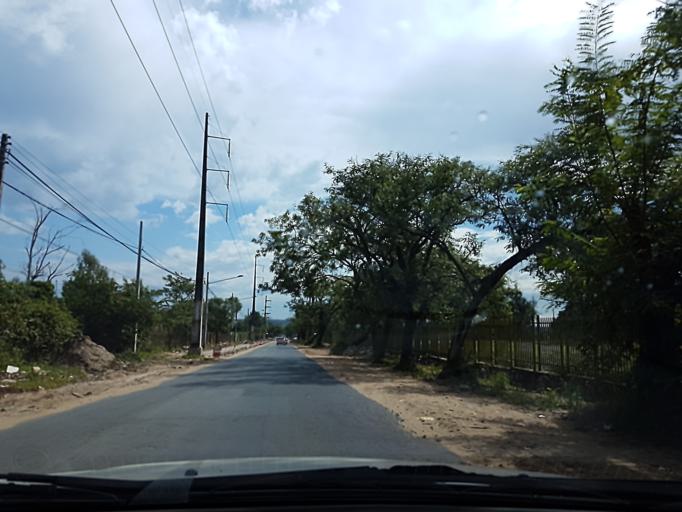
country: PY
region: Asuncion
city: Asuncion
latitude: -25.2459
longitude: -57.5785
